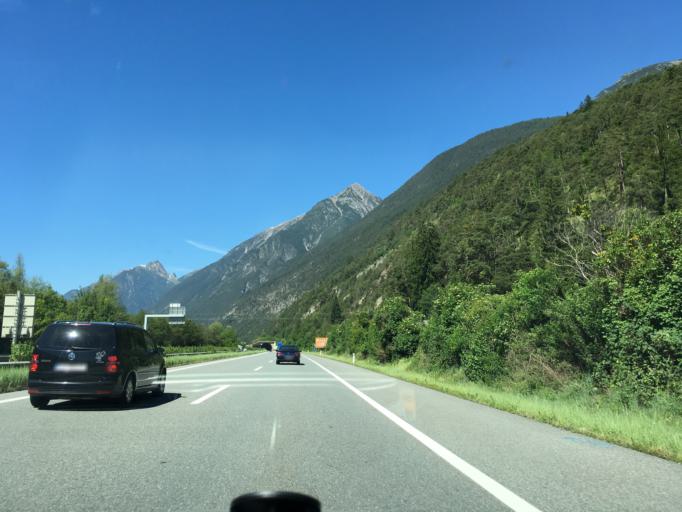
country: AT
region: Tyrol
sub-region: Politischer Bezirk Imst
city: Imsterberg
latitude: 47.2170
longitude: 10.7199
